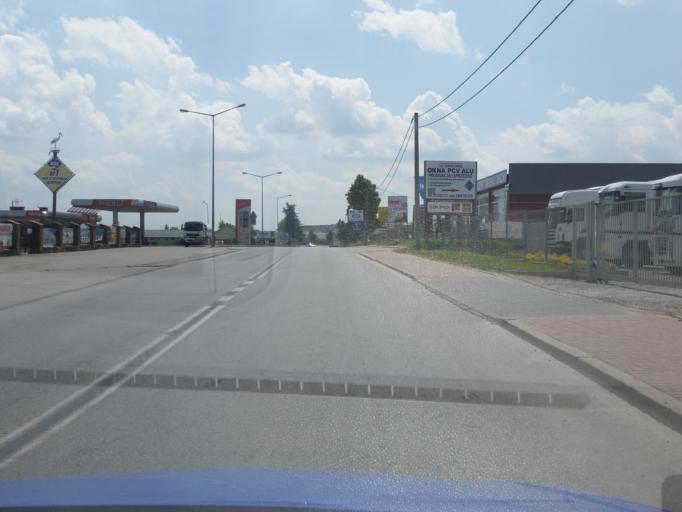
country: PL
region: Swietokrzyskie
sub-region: Powiat kazimierski
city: Kazimierza Wielka
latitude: 50.2783
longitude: 20.4791
